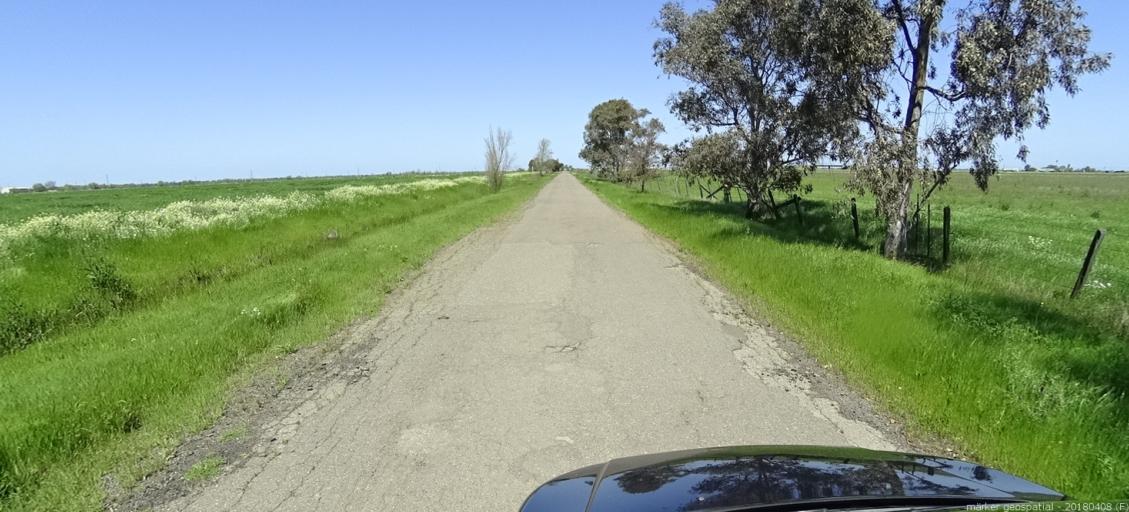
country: US
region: California
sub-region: Sacramento County
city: Laguna
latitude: 38.3670
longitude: -121.4821
